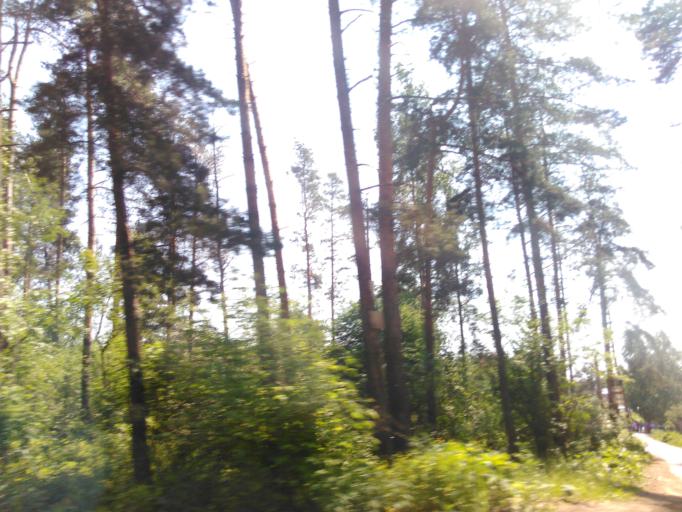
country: RU
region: Moskovskaya
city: Vishnyakovskiye Dachi
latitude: 55.7993
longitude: 38.1433
